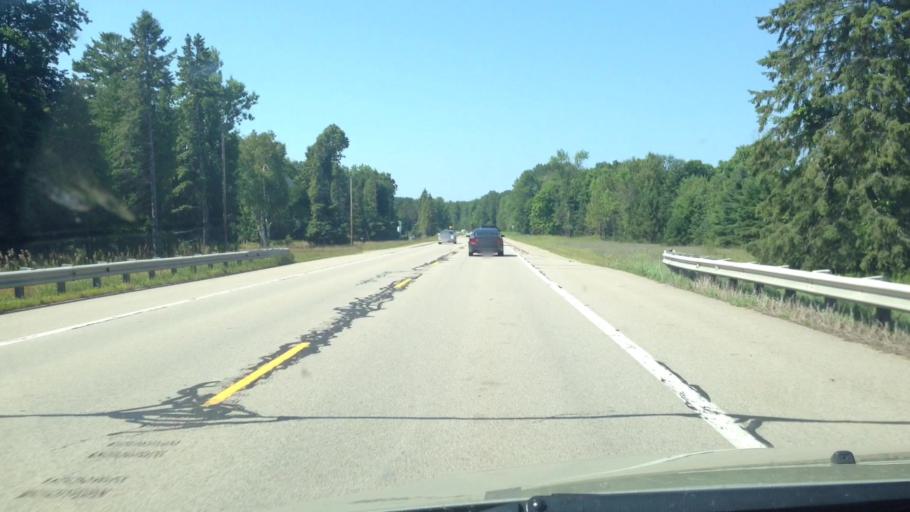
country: US
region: Michigan
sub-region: Menominee County
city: Menominee
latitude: 45.3727
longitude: -87.3895
